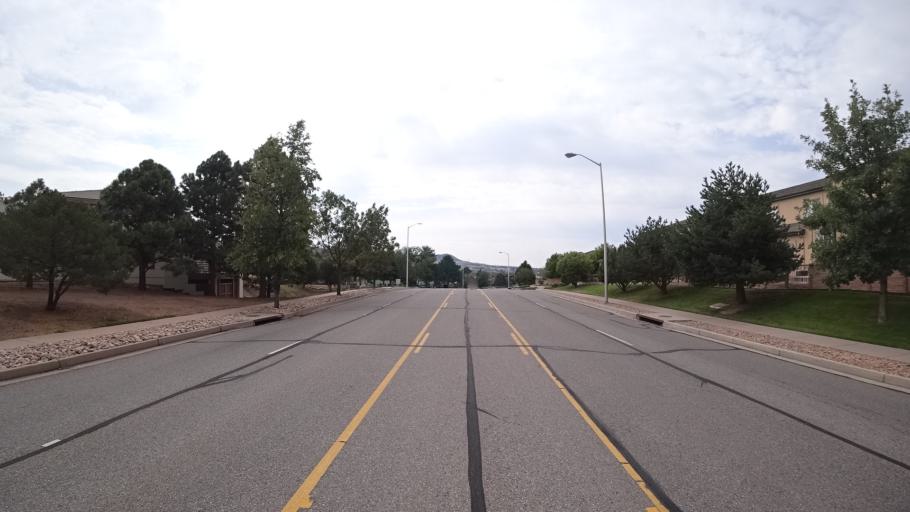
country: US
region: Colorado
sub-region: El Paso County
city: Air Force Academy
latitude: 38.9188
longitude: -104.8254
